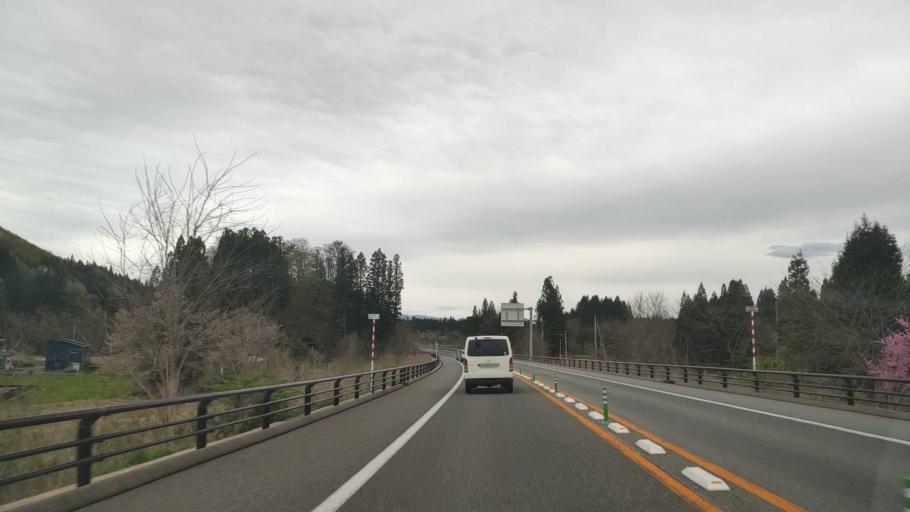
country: JP
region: Akita
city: Odate
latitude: 40.3158
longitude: 140.5824
